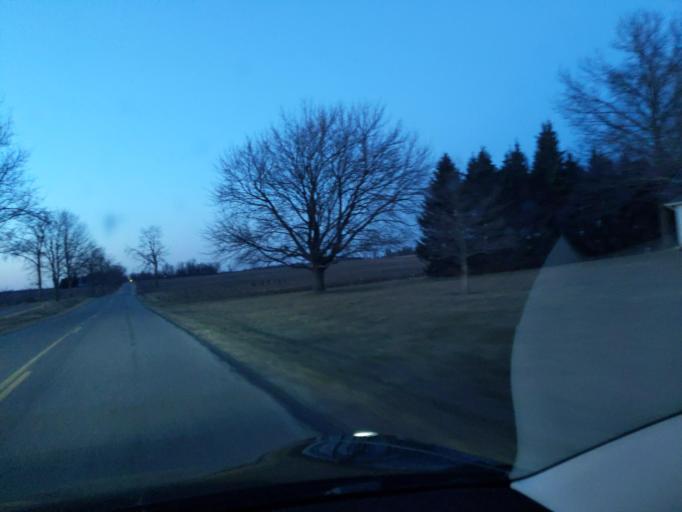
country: US
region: Michigan
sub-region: Ingham County
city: Stockbridge
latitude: 42.5254
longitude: -84.2204
